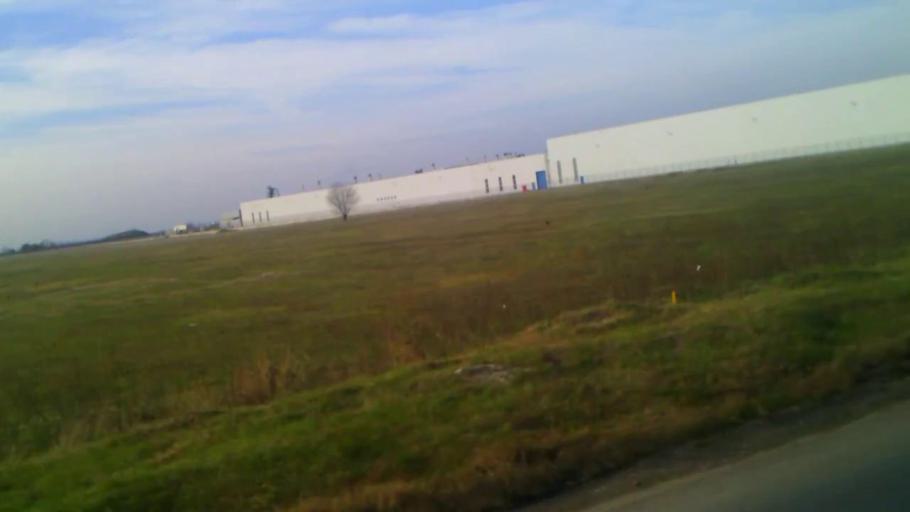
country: RO
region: Ilfov
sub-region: Comuna Berceni
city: Berceni
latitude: 44.3440
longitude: 26.1621
